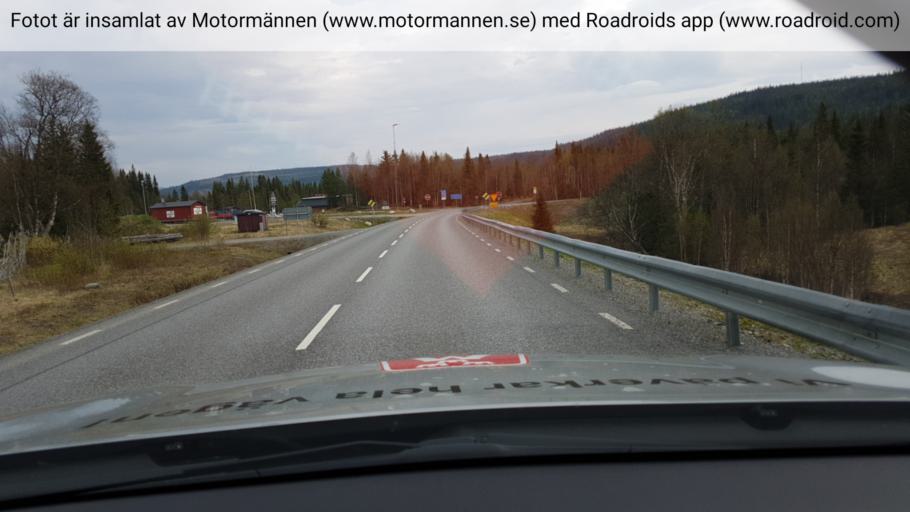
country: SE
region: Jaemtland
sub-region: Are Kommun
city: Are
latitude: 63.4009
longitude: 12.8259
